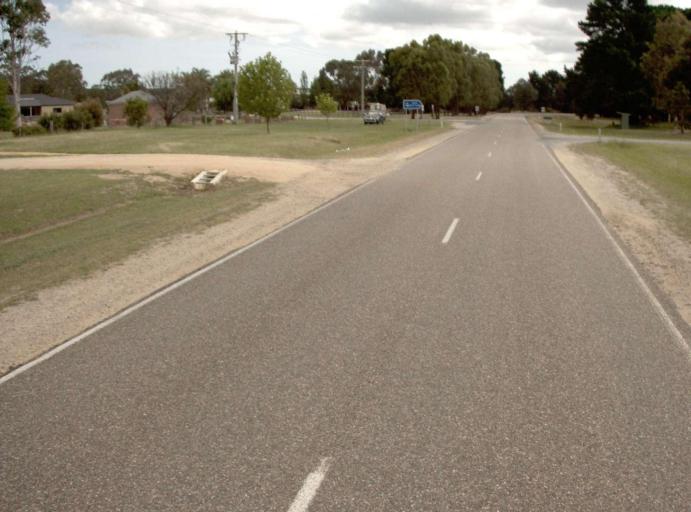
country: AU
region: Victoria
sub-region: Wellington
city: Sale
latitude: -38.1613
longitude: 147.0766
